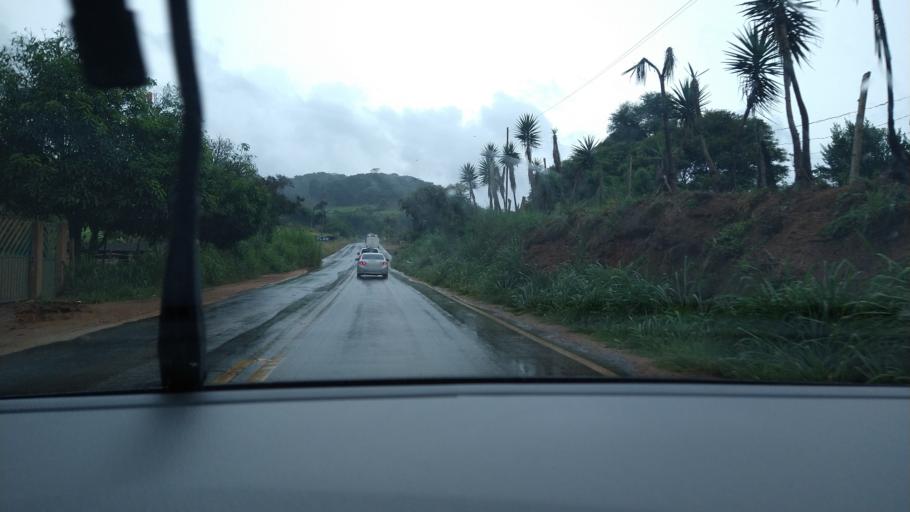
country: BR
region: Minas Gerais
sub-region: Vicosa
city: Vicosa
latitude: -20.6305
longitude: -42.8695
